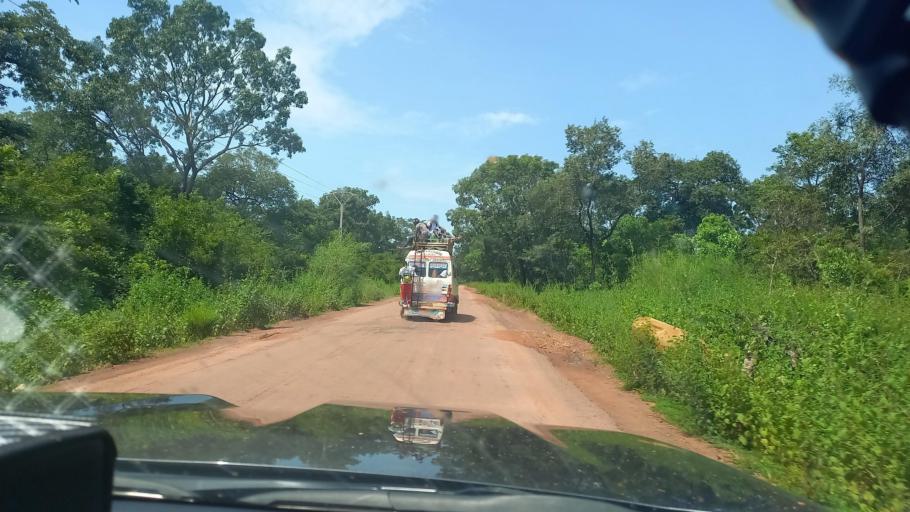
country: SN
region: Kolda
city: Marsassoum
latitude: 12.8575
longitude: -16.1022
